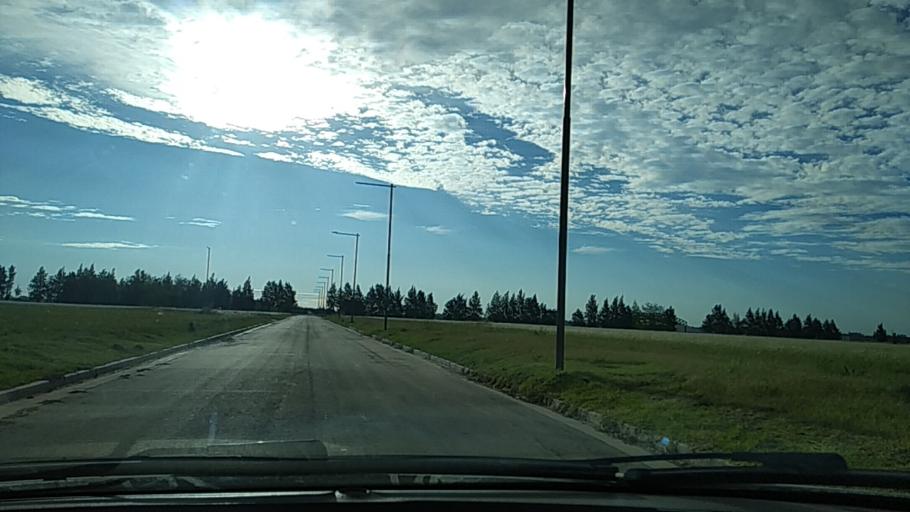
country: AR
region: Santa Fe
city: Perez
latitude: -32.9467
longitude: -60.7657
